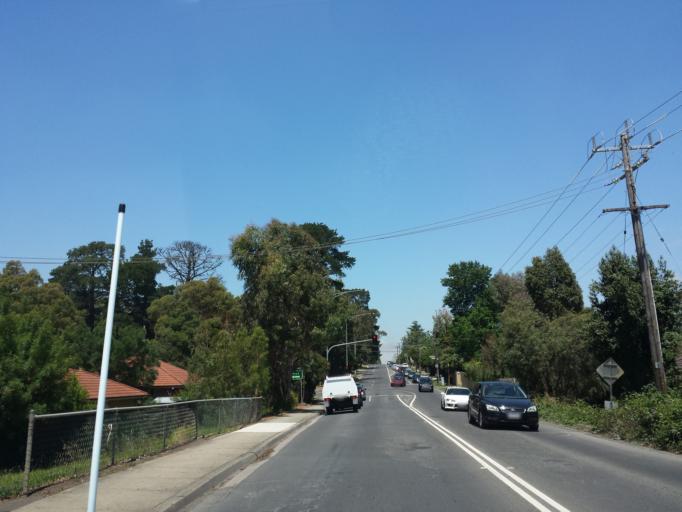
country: AU
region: Victoria
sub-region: Maroondah
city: Croydon North
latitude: -37.7871
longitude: 145.2923
